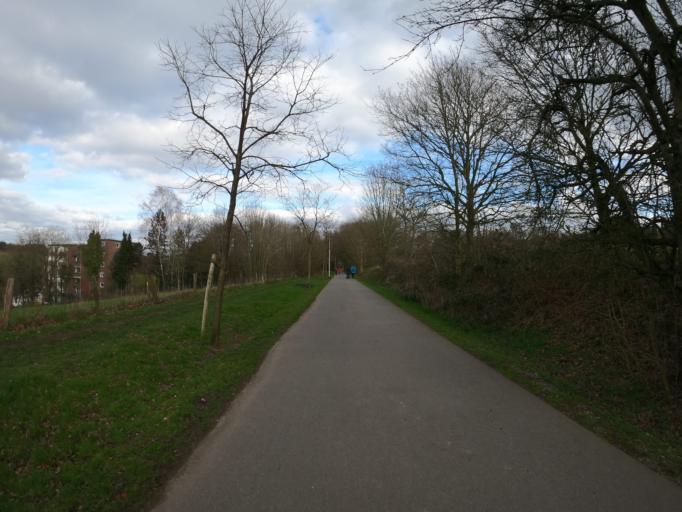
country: DE
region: North Rhine-Westphalia
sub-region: Regierungsbezirk Dusseldorf
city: Solingen
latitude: 51.1953
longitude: 7.0612
